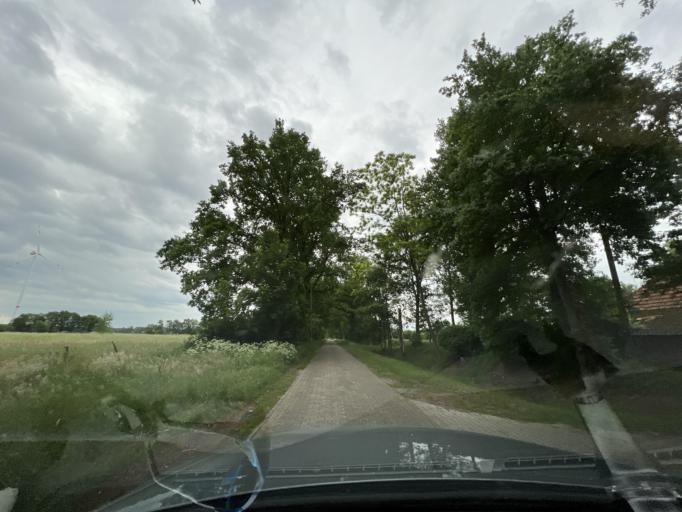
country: DE
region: Lower Saxony
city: Hatten
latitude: 53.0426
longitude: 8.3151
